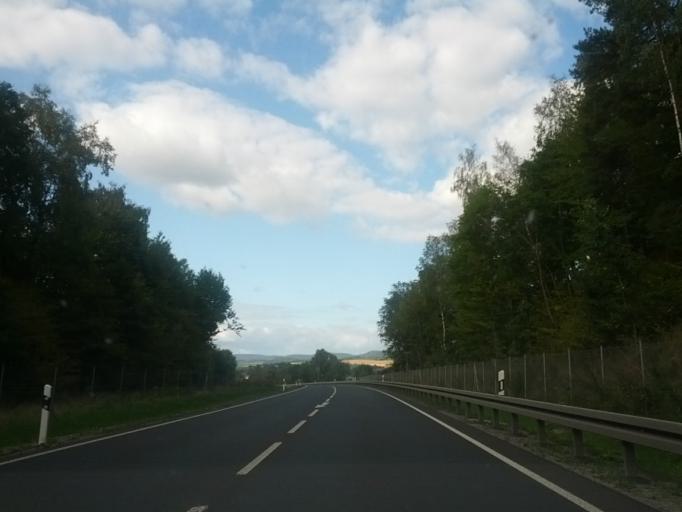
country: DE
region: Thuringia
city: Fambach
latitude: 50.7201
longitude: 10.3693
